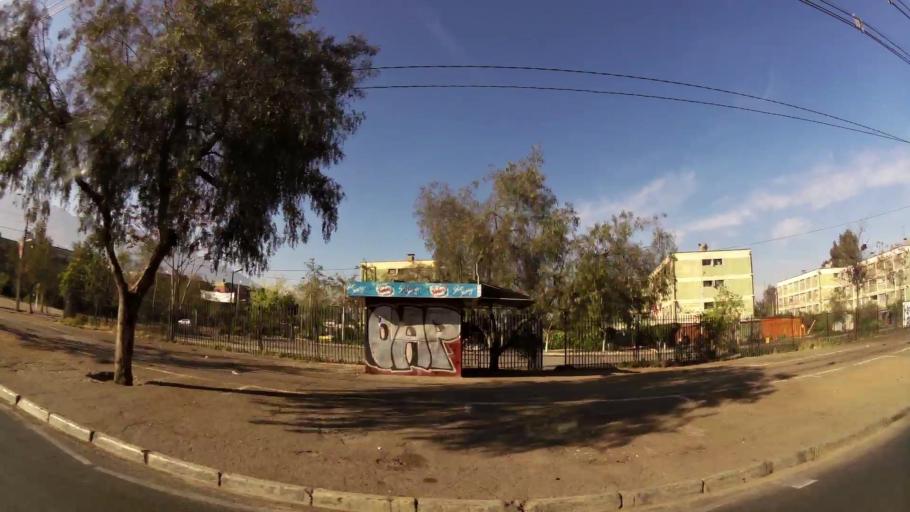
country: CL
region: Santiago Metropolitan
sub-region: Provincia de Santiago
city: Villa Presidente Frei, Nunoa, Santiago, Chile
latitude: -33.4626
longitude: -70.5539
